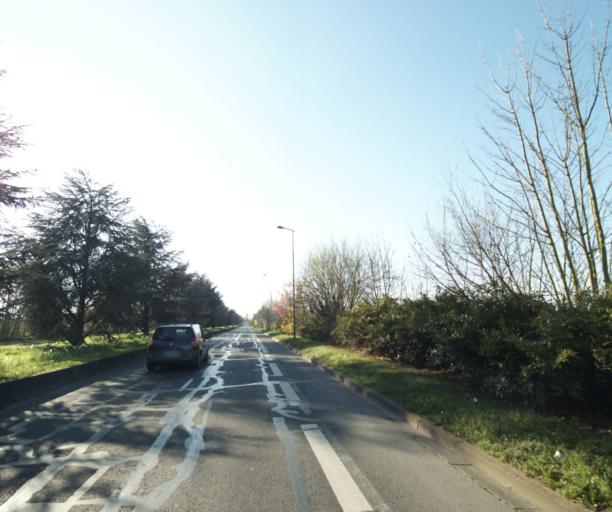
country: FR
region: Ile-de-France
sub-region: Departement du Val-d'Oise
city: Osny
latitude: 49.0474
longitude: 2.0546
